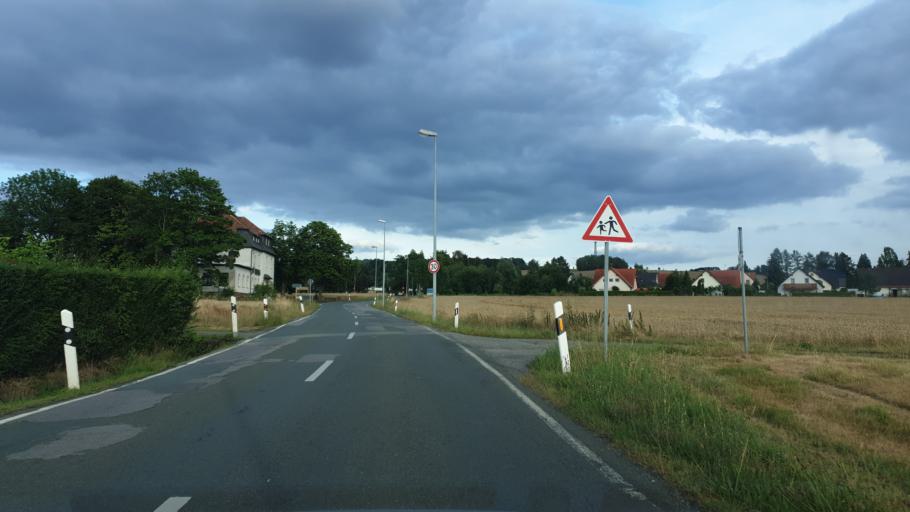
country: DE
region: Saxony
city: Hilbersdorf
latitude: 50.8259
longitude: 12.9788
